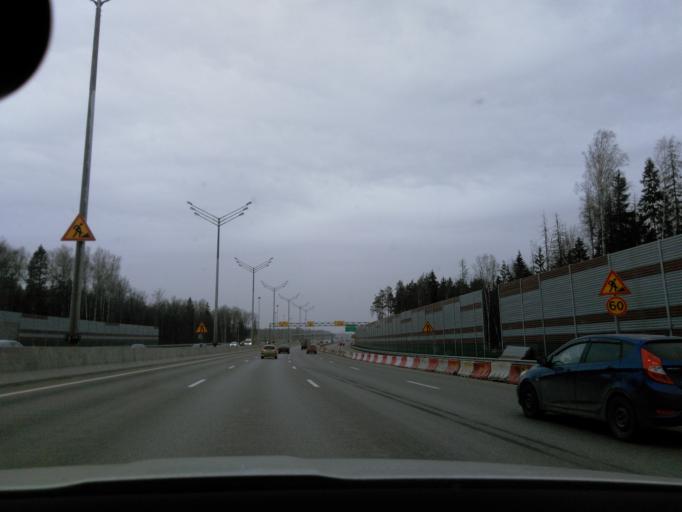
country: RU
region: Moscow
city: Khimki
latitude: 55.9418
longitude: 37.4476
